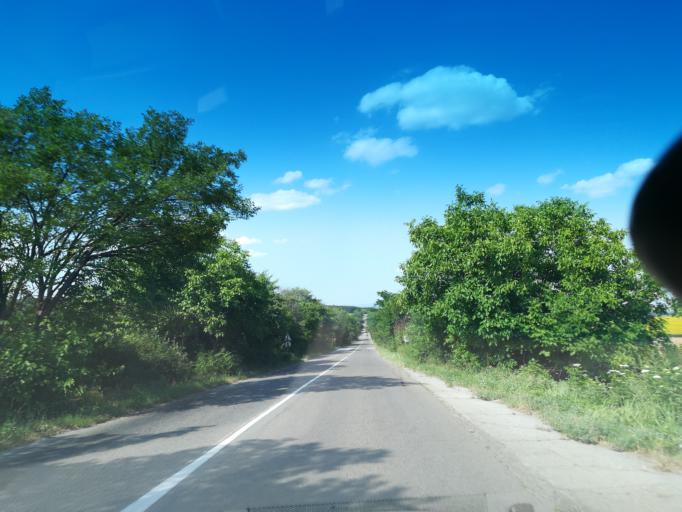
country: BG
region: Stara Zagora
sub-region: Obshtina Chirpan
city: Chirpan
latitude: 42.2214
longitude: 25.3854
